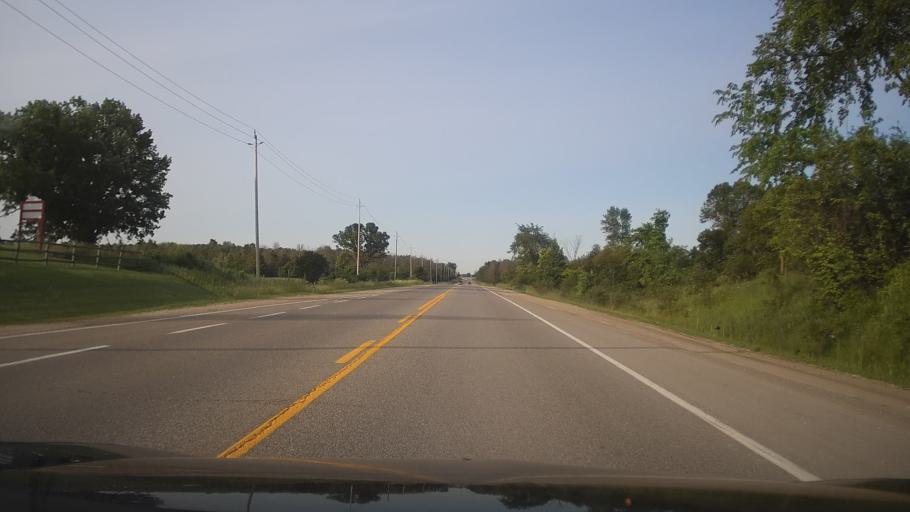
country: CA
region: Ontario
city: Perth
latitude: 44.9532
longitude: -76.2350
